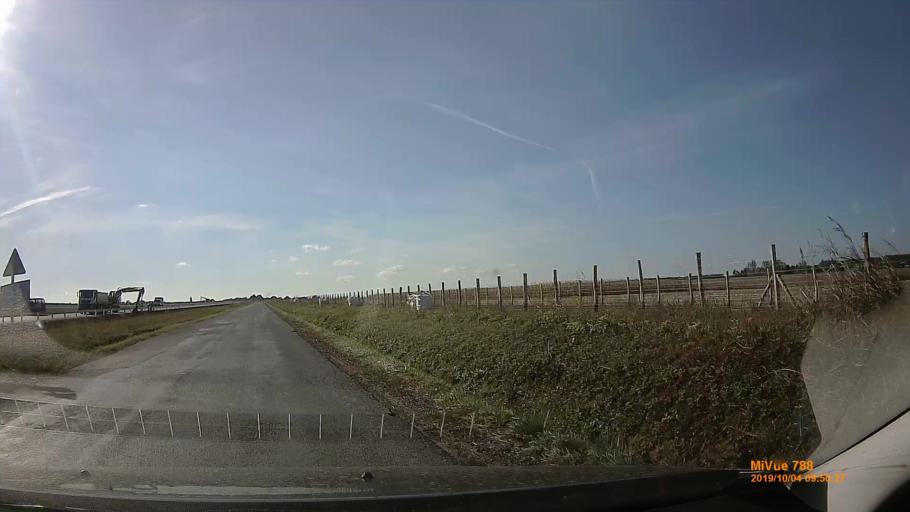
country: HU
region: Somogy
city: Kaposvar
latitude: 46.4354
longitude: 17.7714
